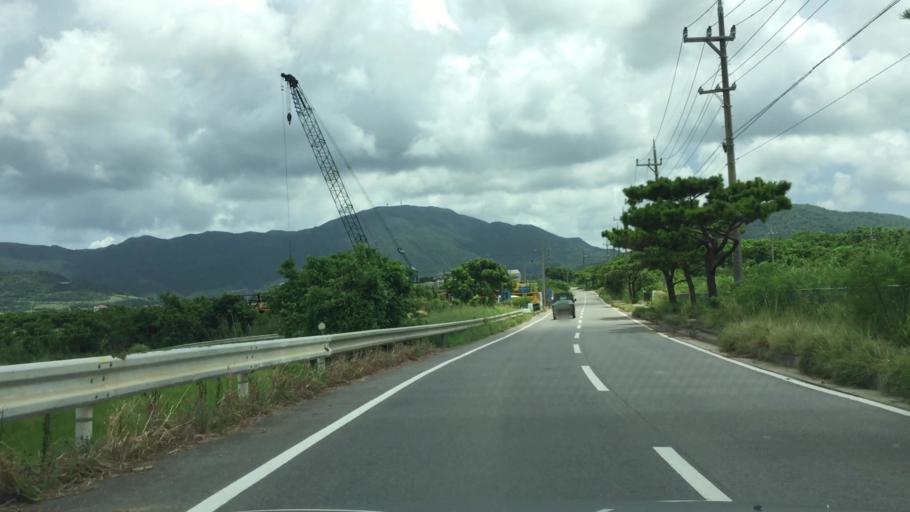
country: JP
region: Okinawa
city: Ishigaki
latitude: 24.3882
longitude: 124.1525
